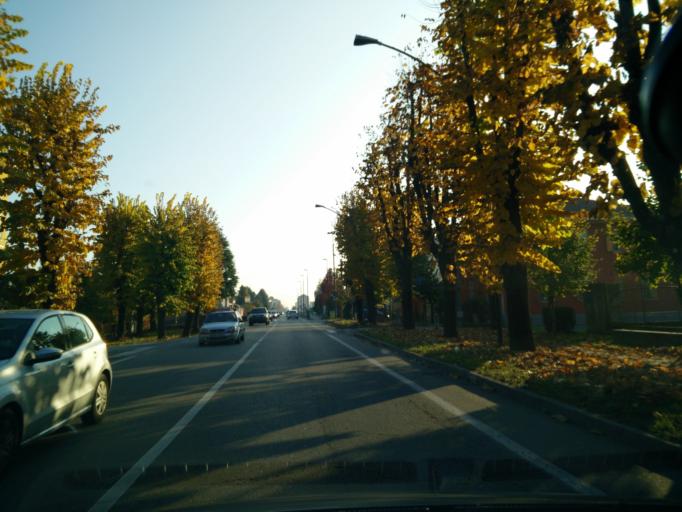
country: IT
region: Piedmont
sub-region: Provincia di Torino
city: Leini
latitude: 45.1766
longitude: 7.7143
